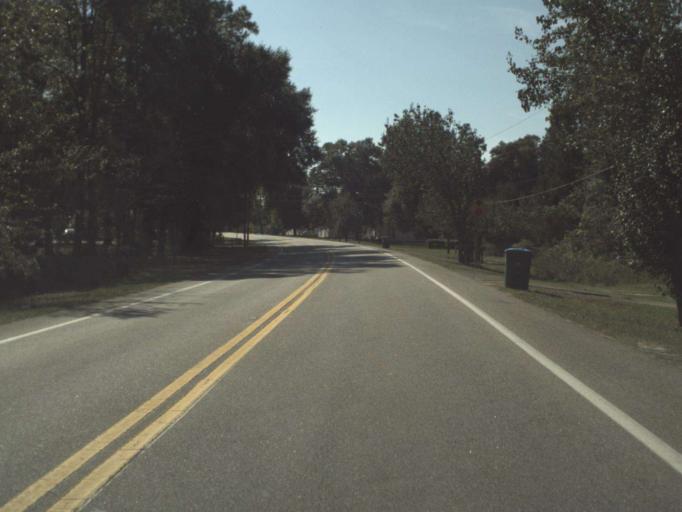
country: US
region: Florida
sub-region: Liberty County
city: Bristol
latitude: 30.4353
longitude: -84.9752
